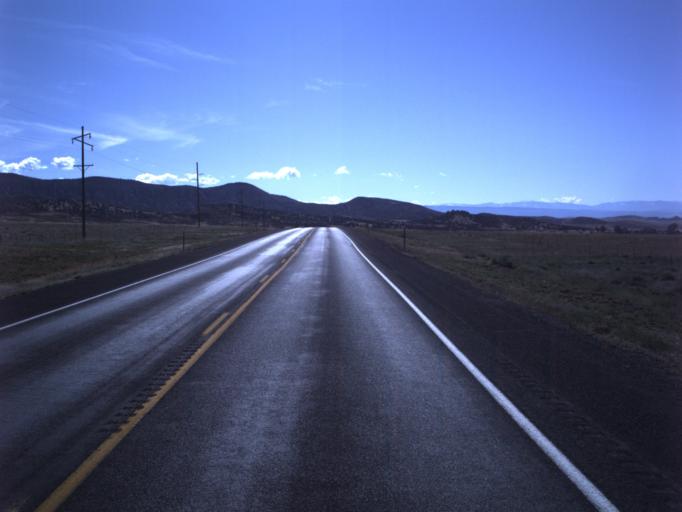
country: US
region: Utah
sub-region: Sanpete County
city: Gunnison
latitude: 39.2467
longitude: -111.8551
